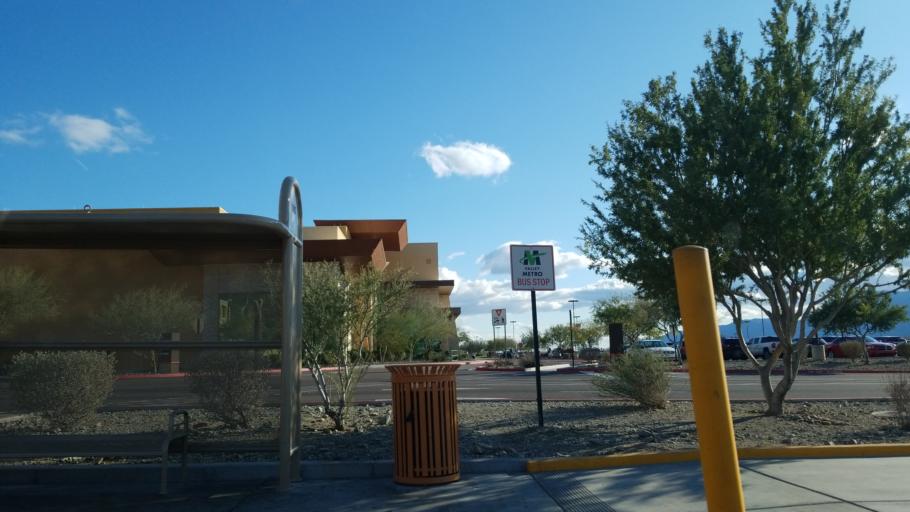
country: US
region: Arizona
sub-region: Maricopa County
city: Laveen
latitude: 33.3109
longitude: -112.1581
